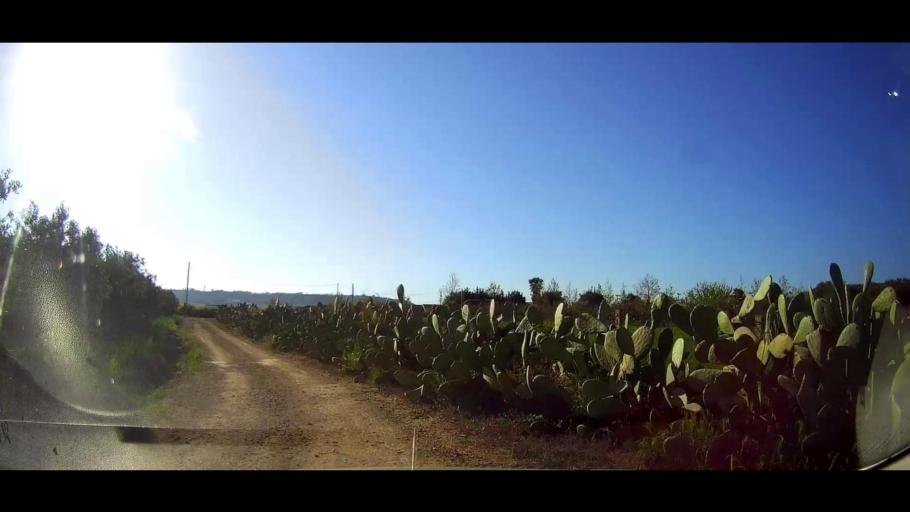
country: IT
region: Calabria
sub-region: Provincia di Crotone
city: Crotone
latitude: 39.0195
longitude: 17.1873
